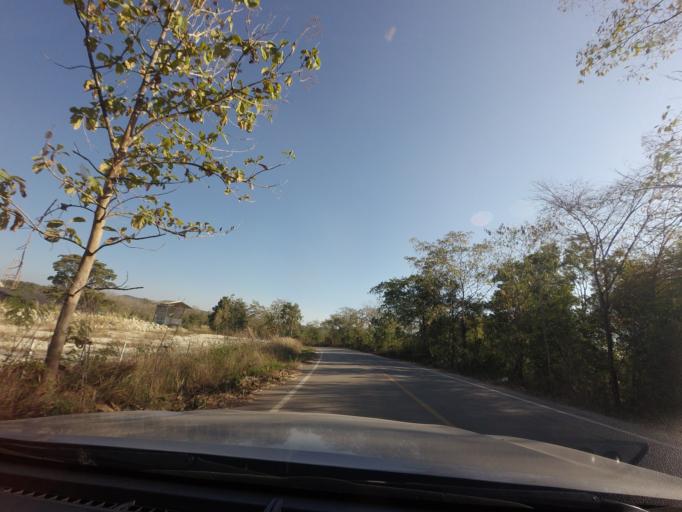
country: TH
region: Lampang
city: Chae Hom
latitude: 18.5317
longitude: 99.6427
